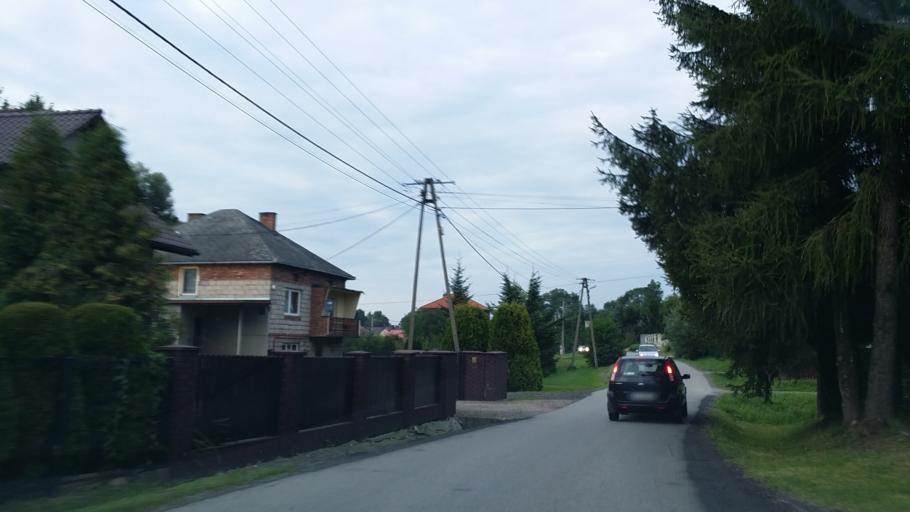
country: PL
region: Lesser Poland Voivodeship
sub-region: Powiat wadowicki
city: Spytkowice
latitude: 49.9903
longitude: 19.5041
